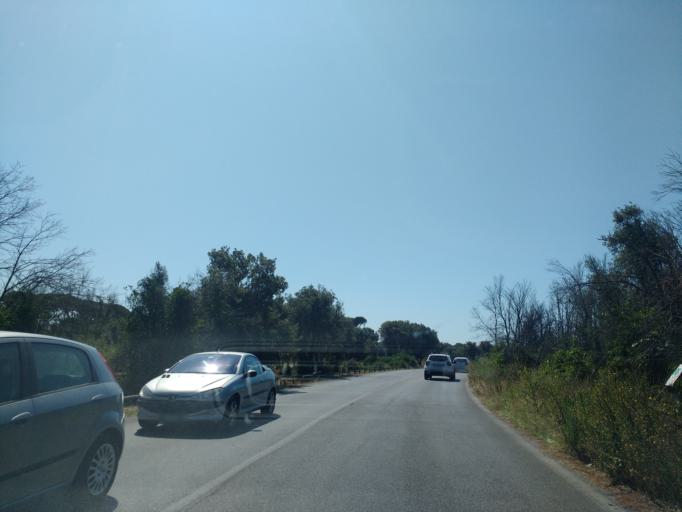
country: IT
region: Latium
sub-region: Citta metropolitana di Roma Capitale
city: Acilia-Castel Fusano-Ostia Antica
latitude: 41.7295
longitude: 12.3383
